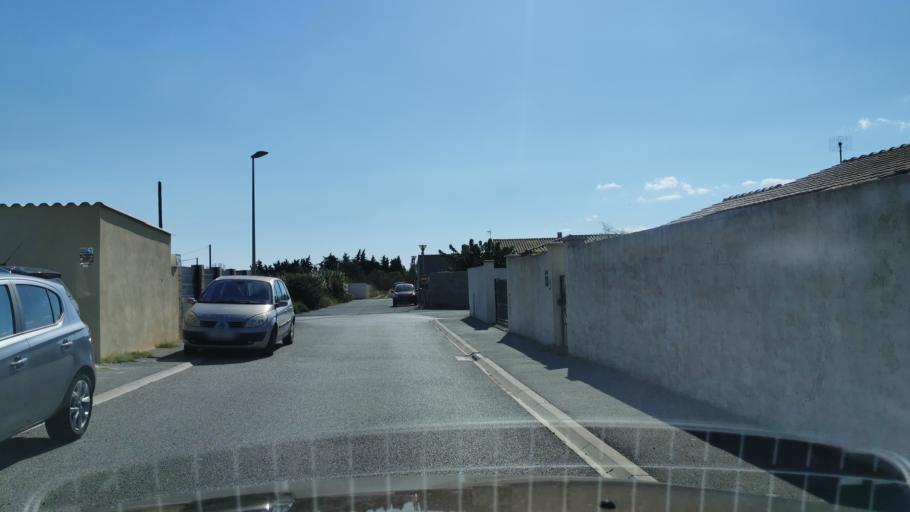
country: FR
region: Languedoc-Roussillon
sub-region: Departement de l'Aude
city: Ginestas
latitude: 43.2503
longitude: 2.8990
